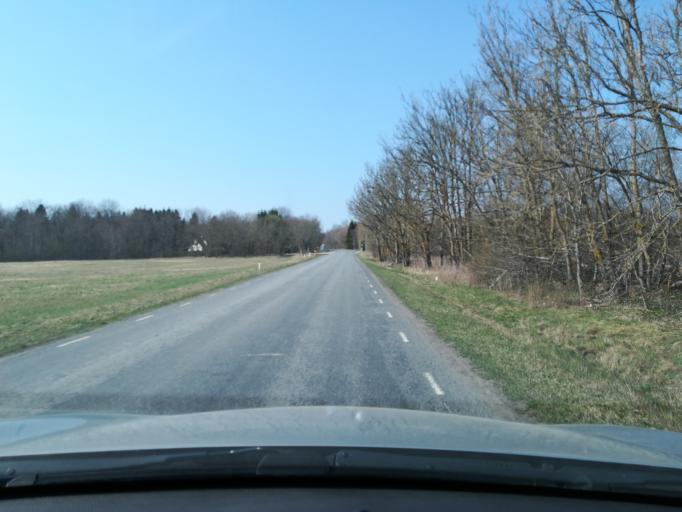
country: EE
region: Harju
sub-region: Harku vald
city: Tabasalu
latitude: 59.4297
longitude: 24.4541
